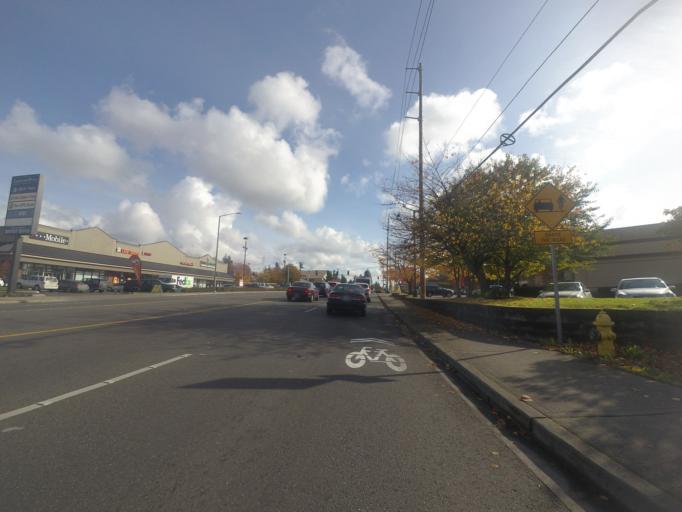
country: US
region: Washington
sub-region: Pierce County
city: Lakewood
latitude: 47.1660
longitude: -122.5092
